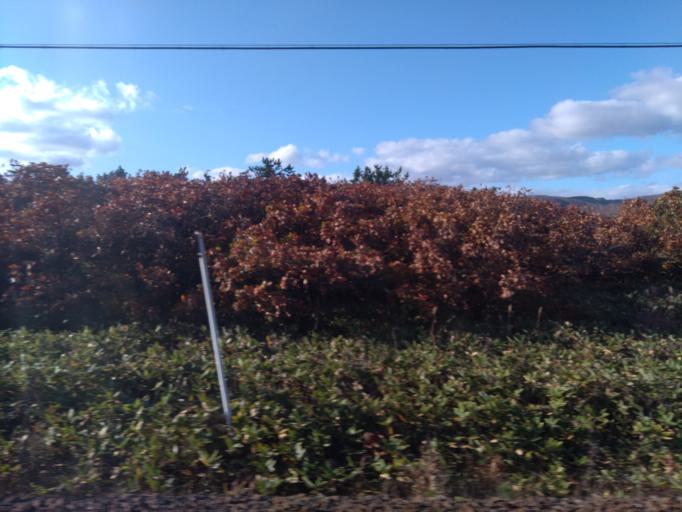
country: JP
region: Hokkaido
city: Niseko Town
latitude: 42.5530
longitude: 140.4207
